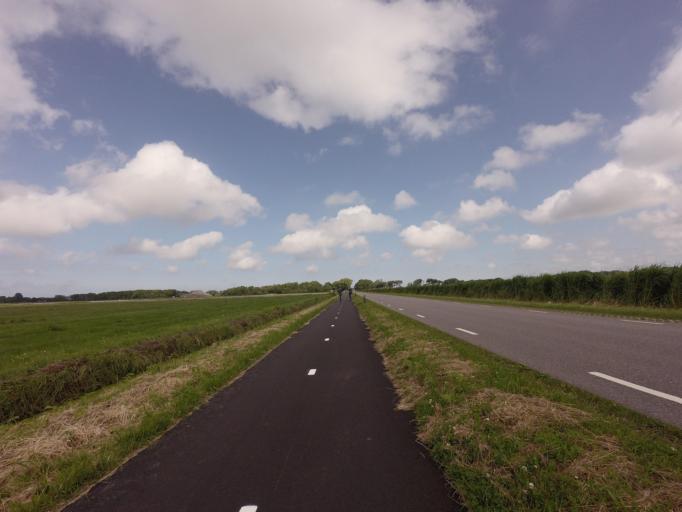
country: NL
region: North Holland
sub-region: Gemeente Schagen
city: Schagen
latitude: 52.8192
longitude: 4.7822
